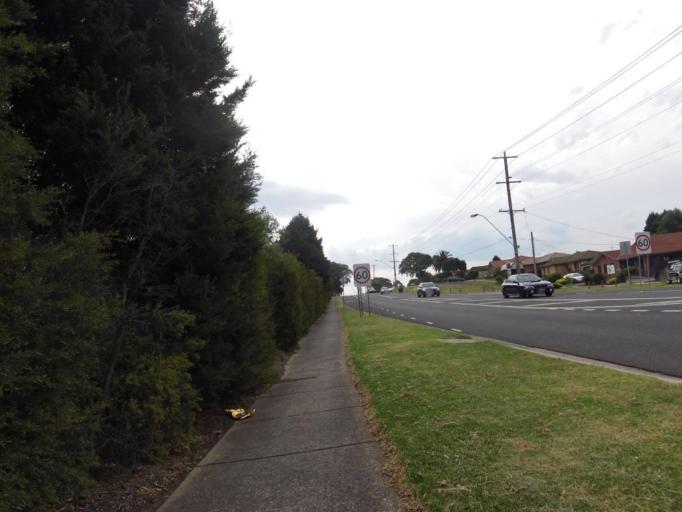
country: AU
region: Victoria
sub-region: Whittlesea
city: Epping
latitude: -37.6476
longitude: 145.0553
